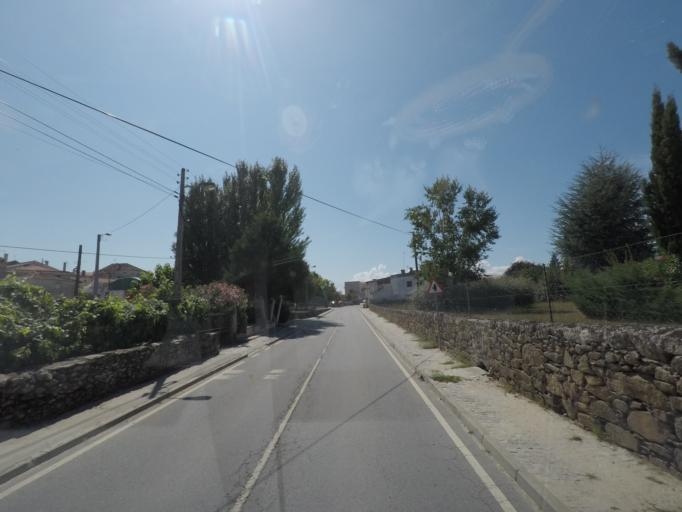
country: PT
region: Vila Real
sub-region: Sabrosa
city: Sabrosa
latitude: 41.2654
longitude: -7.4798
